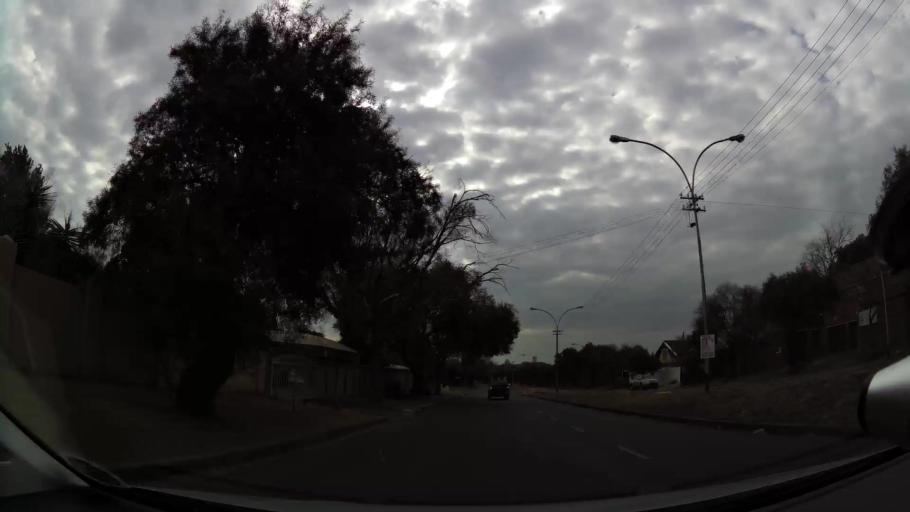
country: ZA
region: Orange Free State
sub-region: Mangaung Metropolitan Municipality
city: Bloemfontein
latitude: -29.0964
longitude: 26.2085
